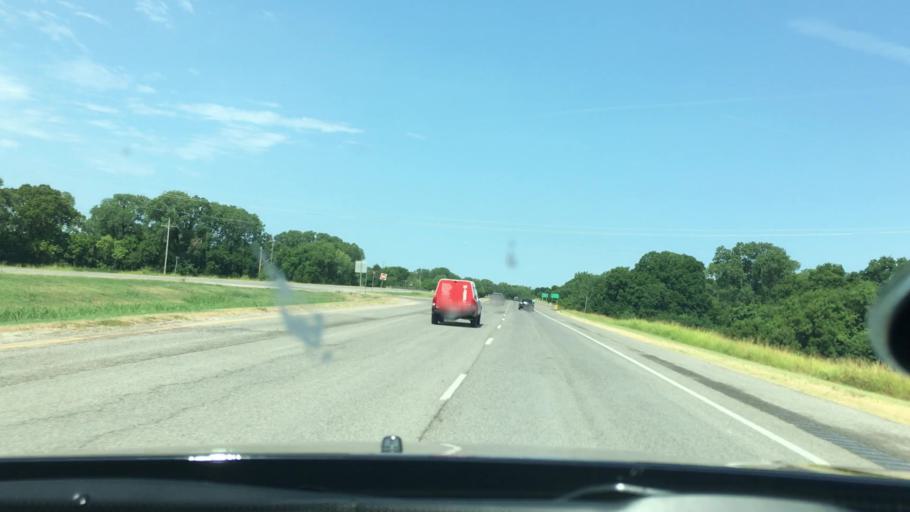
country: US
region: Oklahoma
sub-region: Murray County
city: Davis
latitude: 34.5049
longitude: -97.1372
